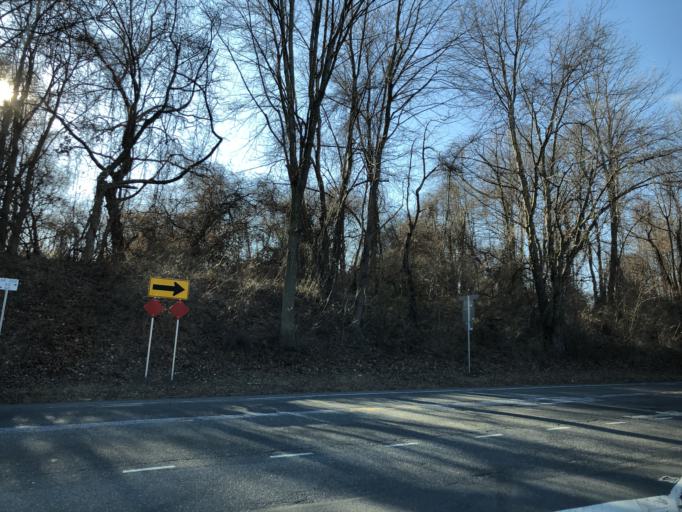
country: US
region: Pennsylvania
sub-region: Delaware County
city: Chester Heights
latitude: 39.8574
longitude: -75.4749
